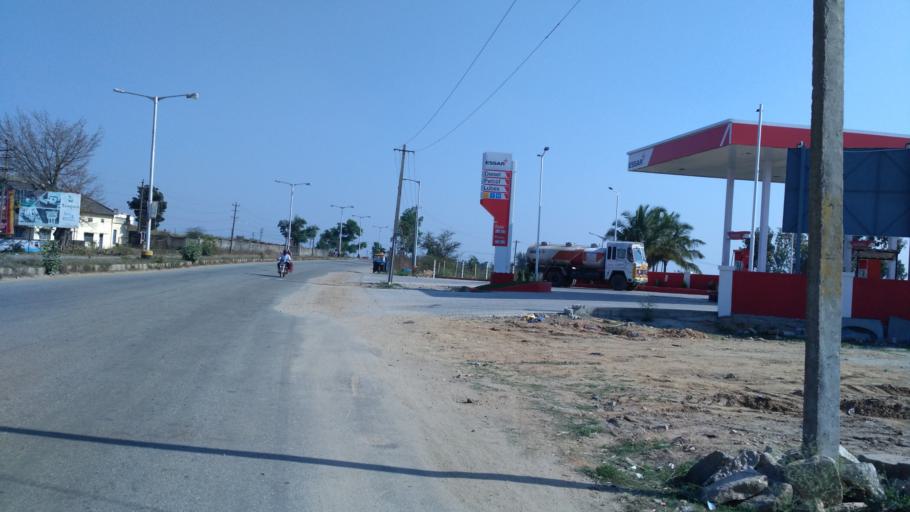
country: IN
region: Karnataka
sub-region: Hassan
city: Hassan
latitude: 12.9709
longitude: 76.1205
